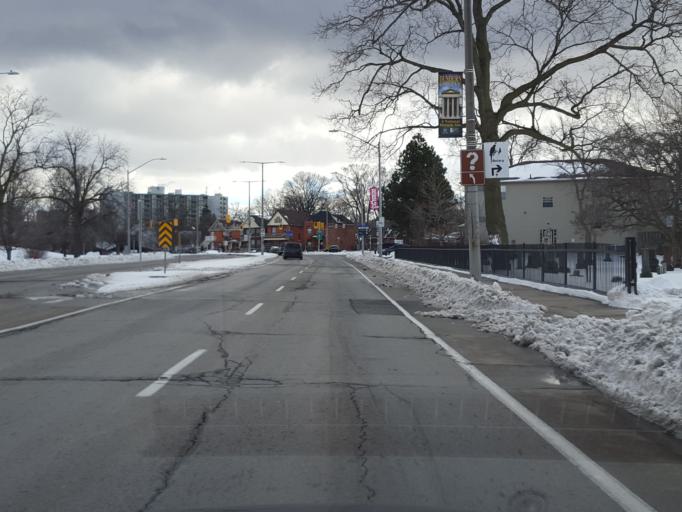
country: CA
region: Ontario
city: Hamilton
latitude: 43.2694
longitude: -79.8860
